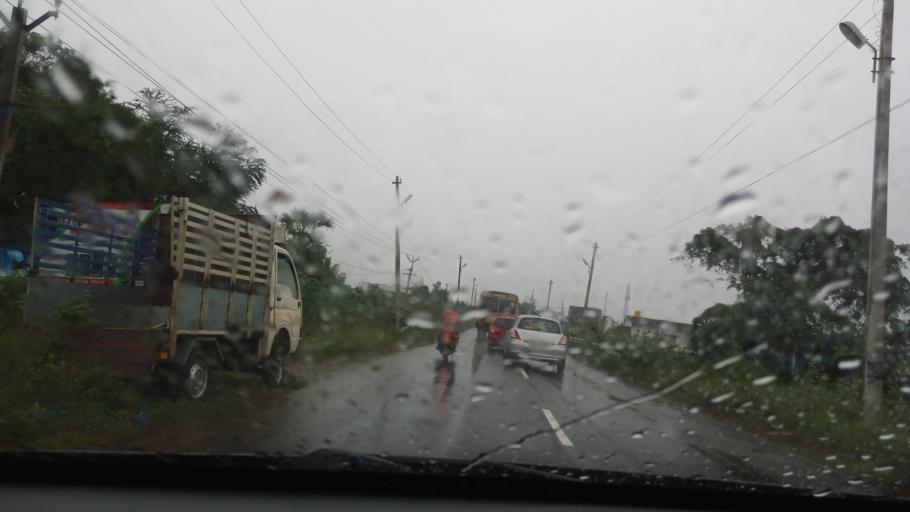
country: IN
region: Tamil Nadu
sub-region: Tiruvannamalai
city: Cheyyar
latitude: 12.6664
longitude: 79.5366
